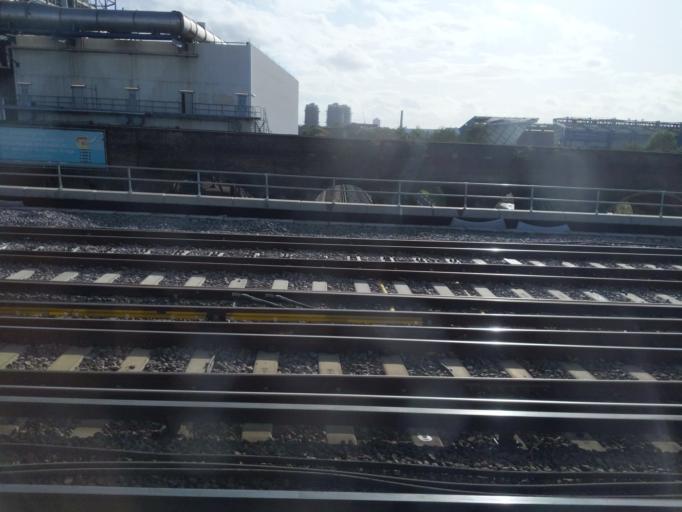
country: GB
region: England
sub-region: Greater London
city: Poplar
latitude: 51.4869
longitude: -0.0475
